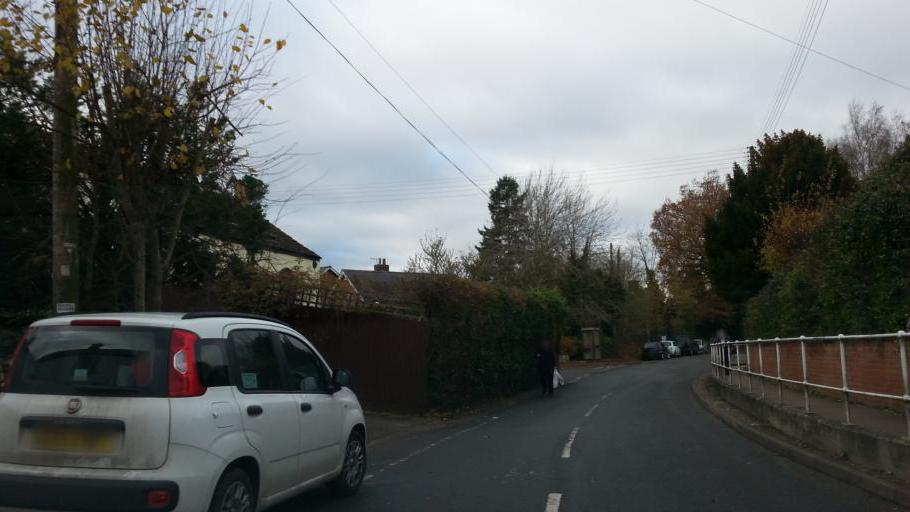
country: GB
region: England
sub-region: Suffolk
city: Ixworth
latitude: 52.3531
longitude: 0.8891
